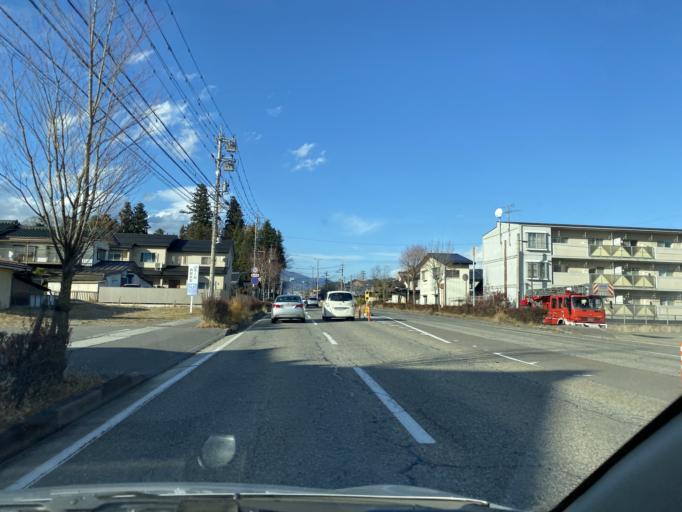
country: JP
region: Nagano
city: Omachi
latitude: 36.5057
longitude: 137.8546
